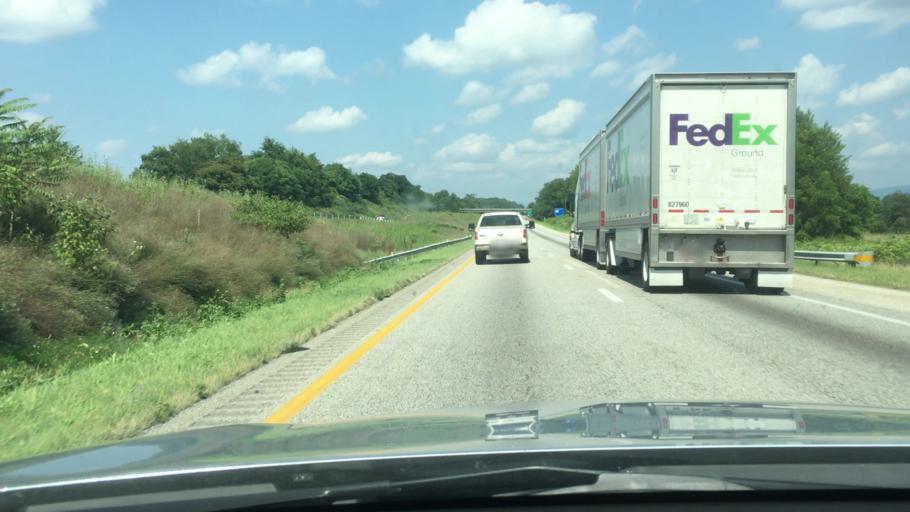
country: US
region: Virginia
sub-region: Rockbridge County
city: Glasgow
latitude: 37.6577
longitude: -79.5357
